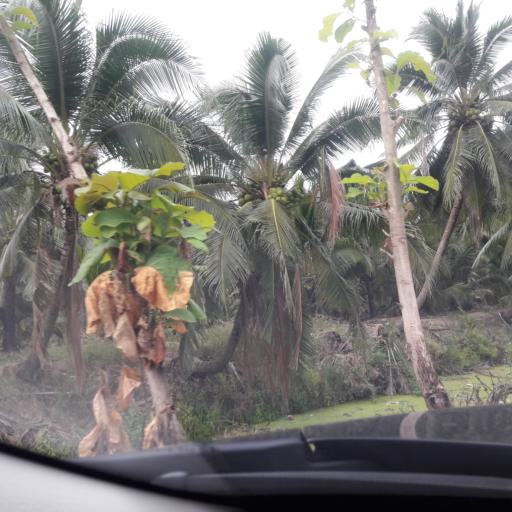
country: TH
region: Ratchaburi
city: Damnoen Saduak
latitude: 13.5750
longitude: 99.9359
